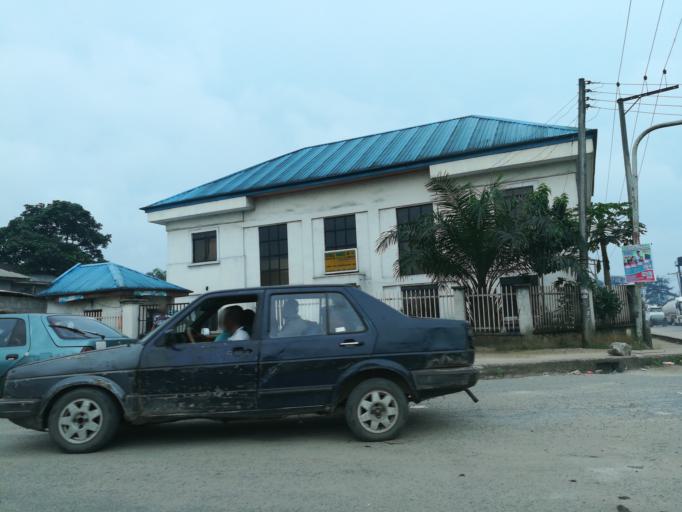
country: NG
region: Rivers
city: Port Harcourt
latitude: 4.7635
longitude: 7.0126
